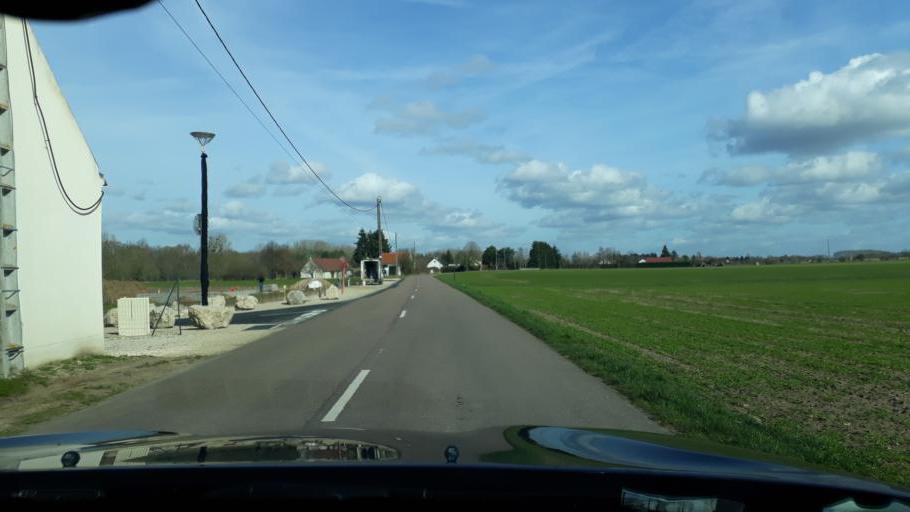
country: FR
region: Centre
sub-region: Departement du Loiret
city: Donnery
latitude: 47.9149
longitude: 2.1098
